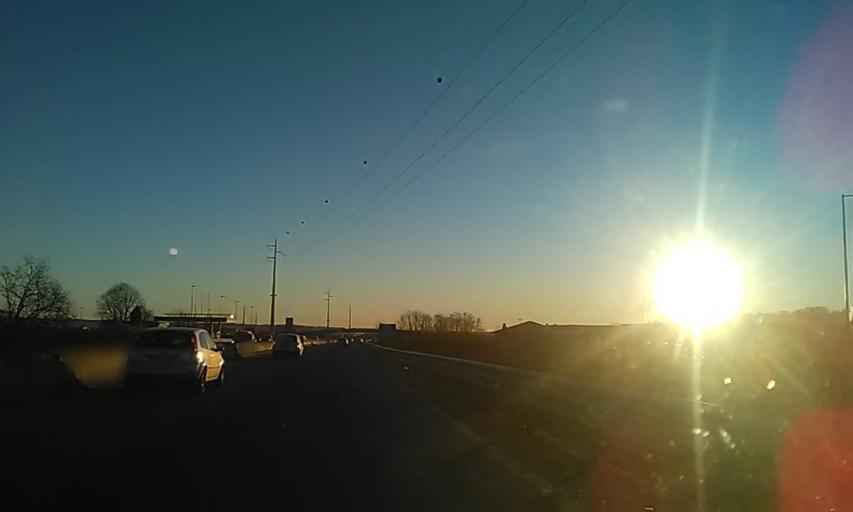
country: IT
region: Piedmont
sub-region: Provincia di Biella
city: Valdengo
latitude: 45.5552
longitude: 8.1291
